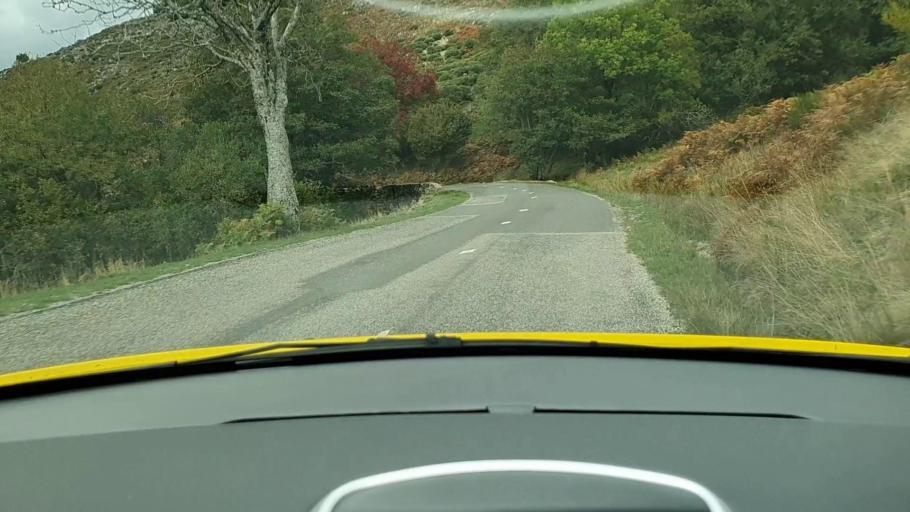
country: FR
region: Languedoc-Roussillon
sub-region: Departement de la Lozere
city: Meyrueis
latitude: 44.0769
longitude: 3.5051
